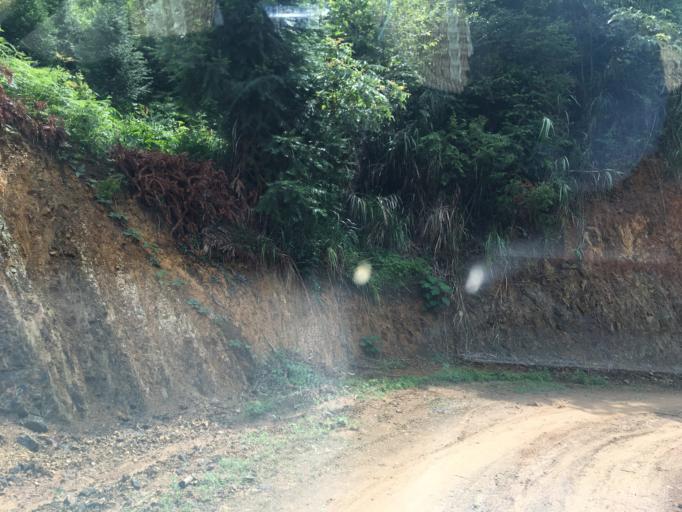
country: CN
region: Guangxi Zhuangzu Zizhiqu
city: Xinzhou
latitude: 24.8670
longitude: 105.8534
